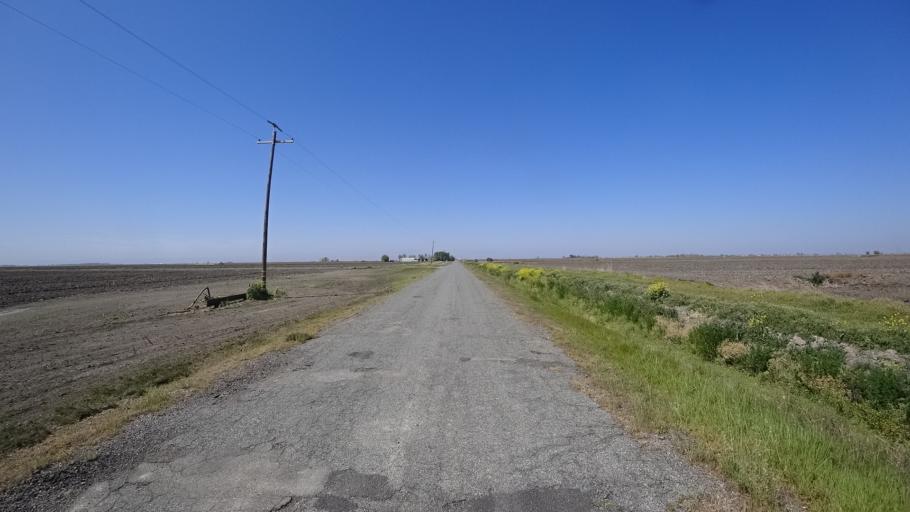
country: US
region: California
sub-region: Glenn County
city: Willows
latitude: 39.4929
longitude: -122.0710
